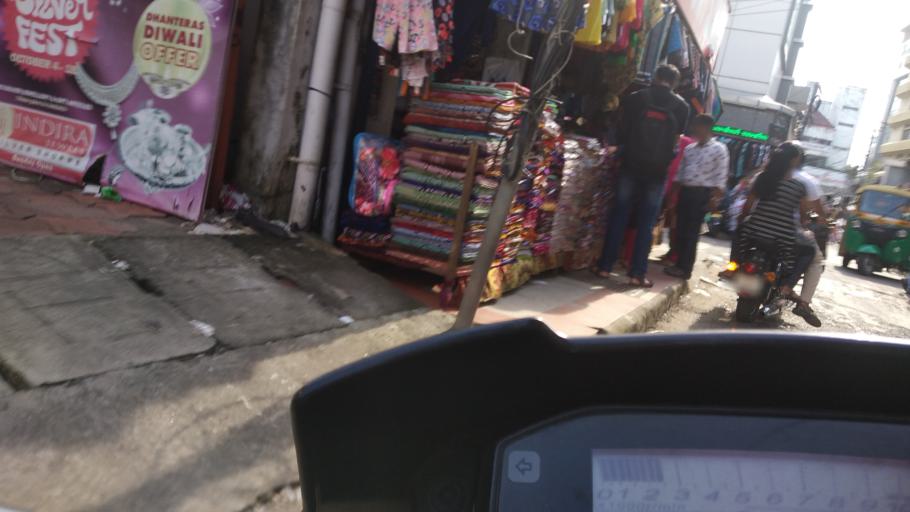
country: IN
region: Kerala
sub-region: Ernakulam
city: Cochin
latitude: 9.9792
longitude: 76.2775
